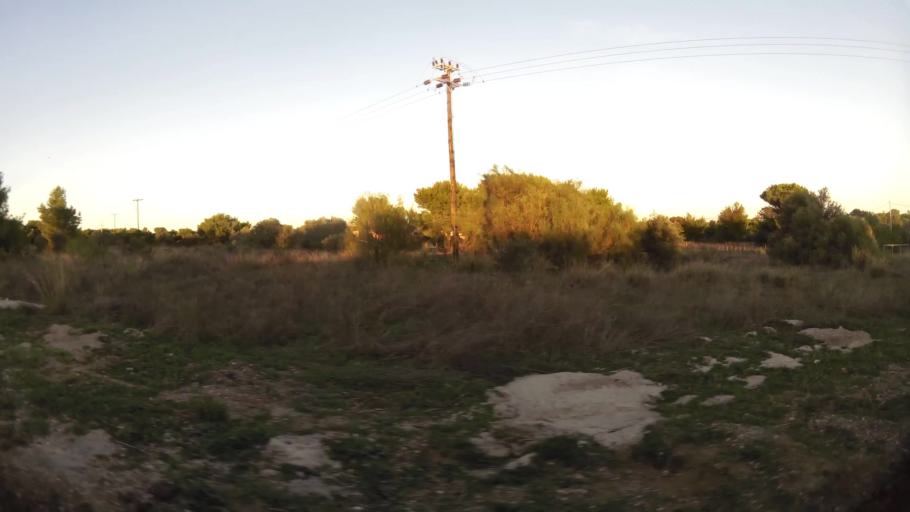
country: GR
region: Attica
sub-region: Nomarchia Anatolikis Attikis
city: Rafina
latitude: 38.0015
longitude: 24.0199
